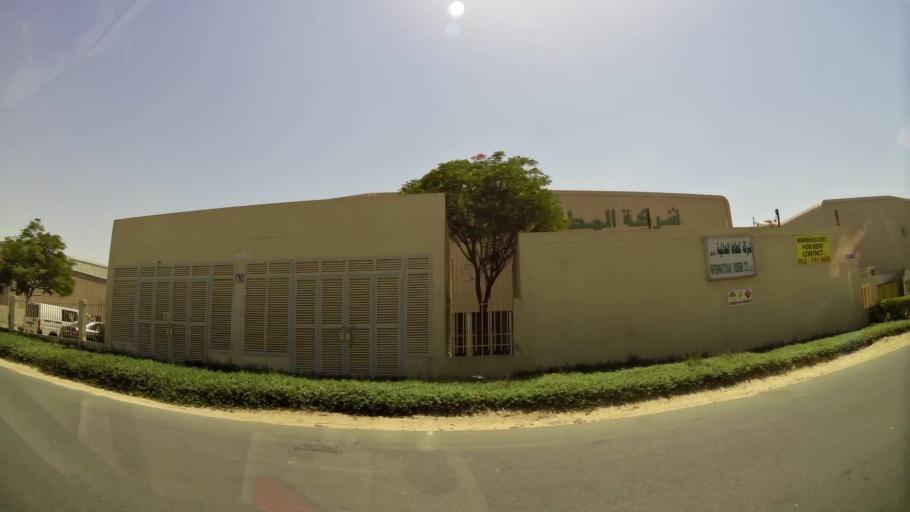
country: AE
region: Dubai
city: Dubai
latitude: 24.9878
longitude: 55.1568
